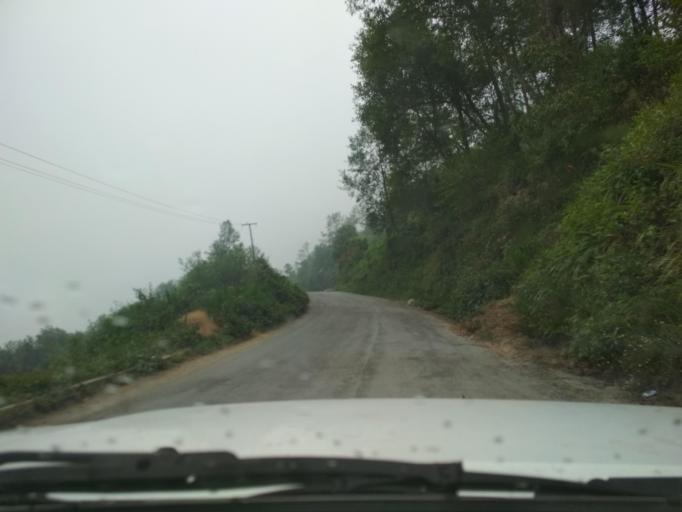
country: MX
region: Veracruz
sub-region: La Perla
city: Metlac Hernandez (Metlac Primero)
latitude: 18.9506
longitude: -97.1653
